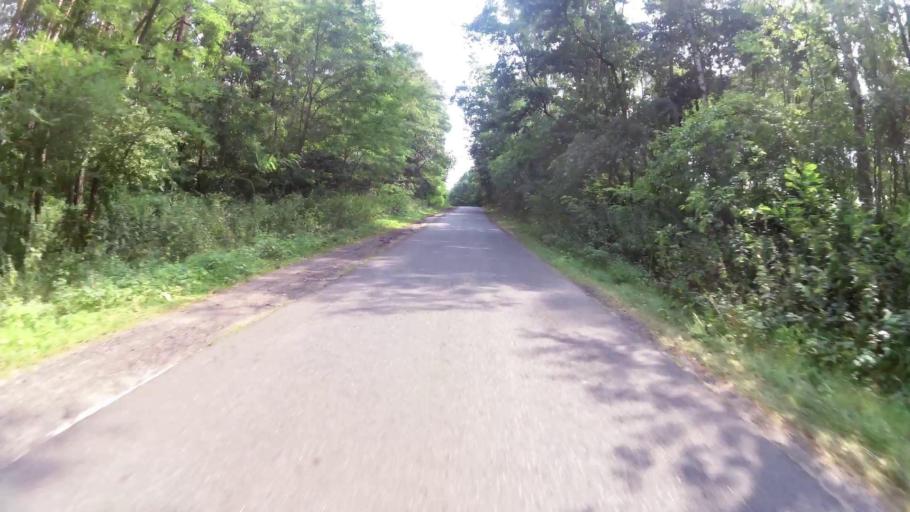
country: PL
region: West Pomeranian Voivodeship
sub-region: Powiat gryfinski
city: Chojna
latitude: 52.9102
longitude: 14.4701
